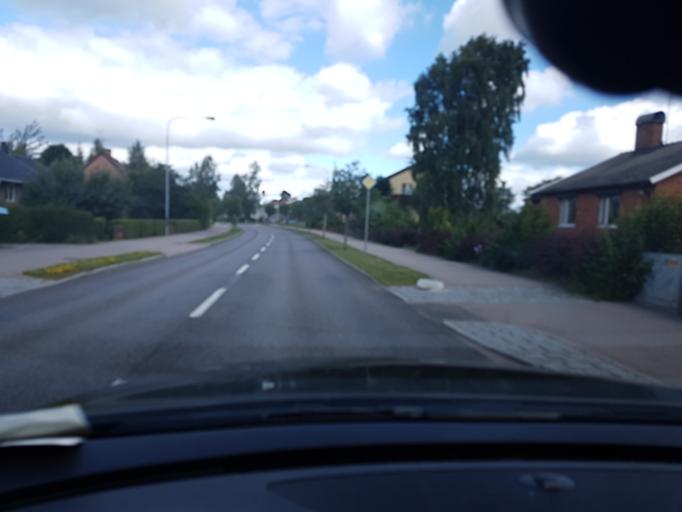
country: SE
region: Kronoberg
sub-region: Lessebo Kommun
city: Lessebo
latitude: 56.7592
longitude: 15.2670
